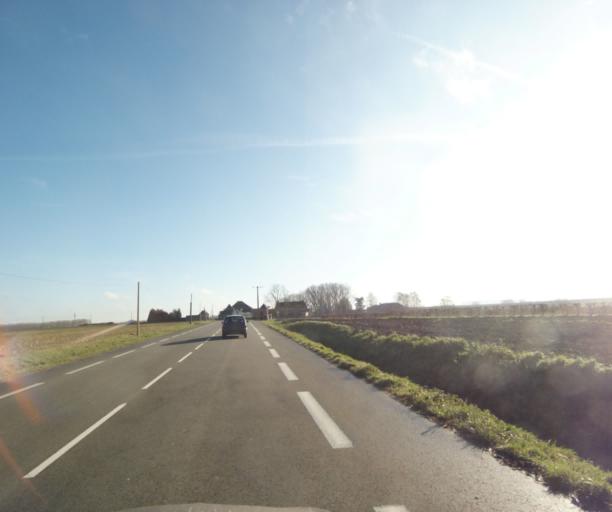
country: FR
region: Nord-Pas-de-Calais
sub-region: Departement du Nord
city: Preseau
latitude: 50.3049
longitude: 3.5859
